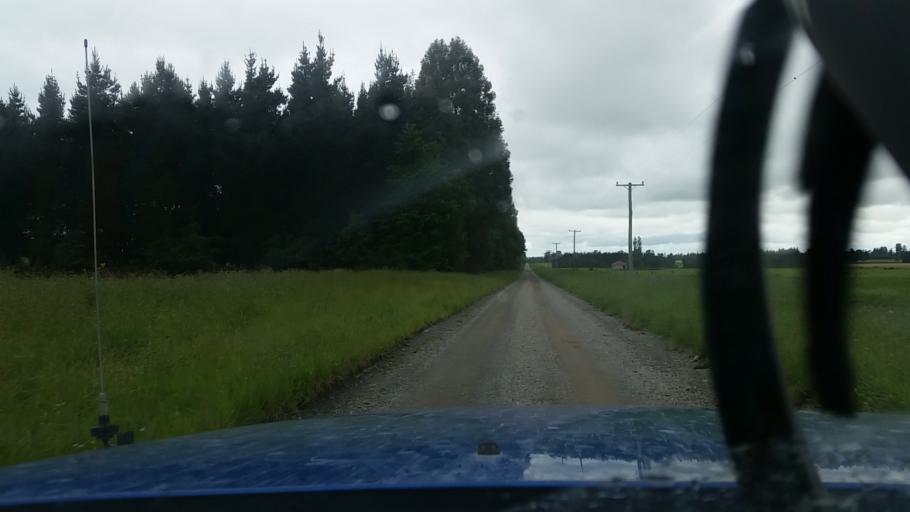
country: NZ
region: Canterbury
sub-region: Ashburton District
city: Methven
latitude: -43.6952
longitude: 171.4119
